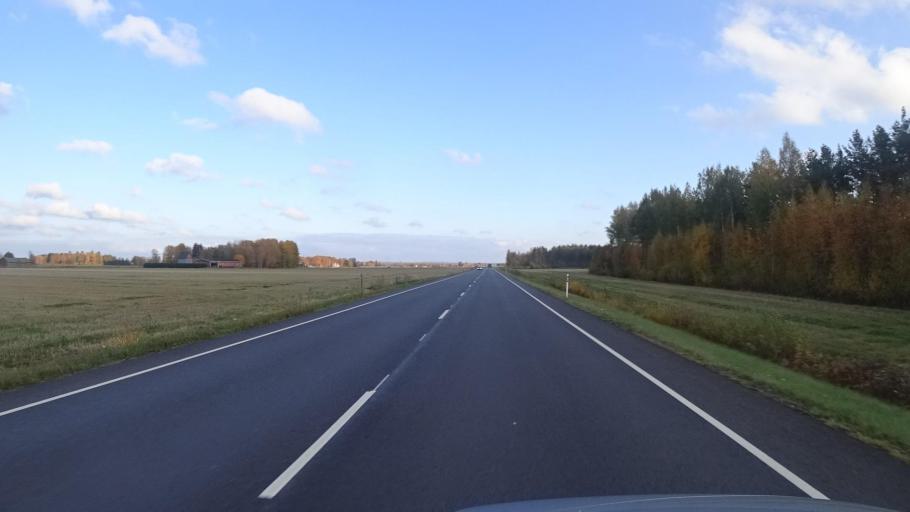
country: FI
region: Satakunta
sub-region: Rauma
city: Koeylioe
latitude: 61.0731
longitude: 22.3023
